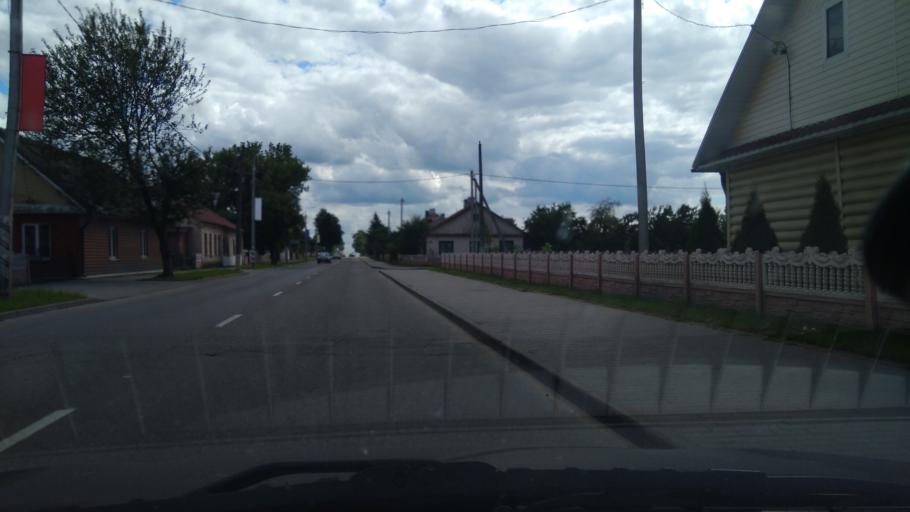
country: BY
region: Grodnenskaya
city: Shchuchin
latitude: 53.6015
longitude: 24.7423
